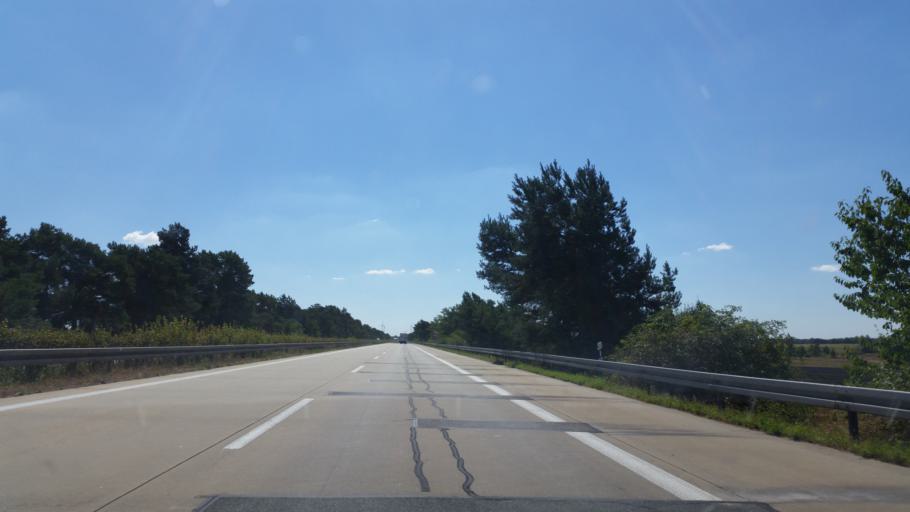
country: DE
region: Brandenburg
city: Vetschau
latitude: 51.8093
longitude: 14.0307
